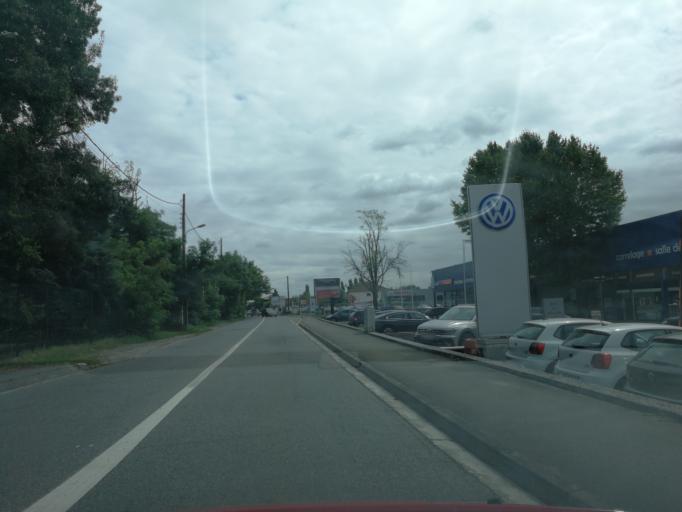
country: FR
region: Midi-Pyrenees
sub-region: Departement de la Haute-Garonne
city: Ramonville-Saint-Agne
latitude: 43.5706
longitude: 1.4986
